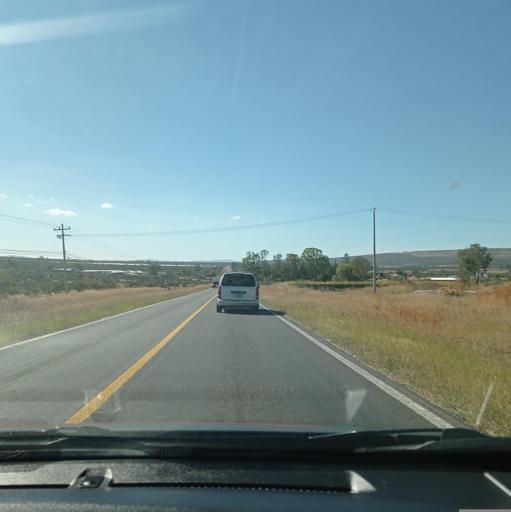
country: MX
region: Jalisco
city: San Miguel el Alto
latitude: 21.0228
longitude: -102.4408
